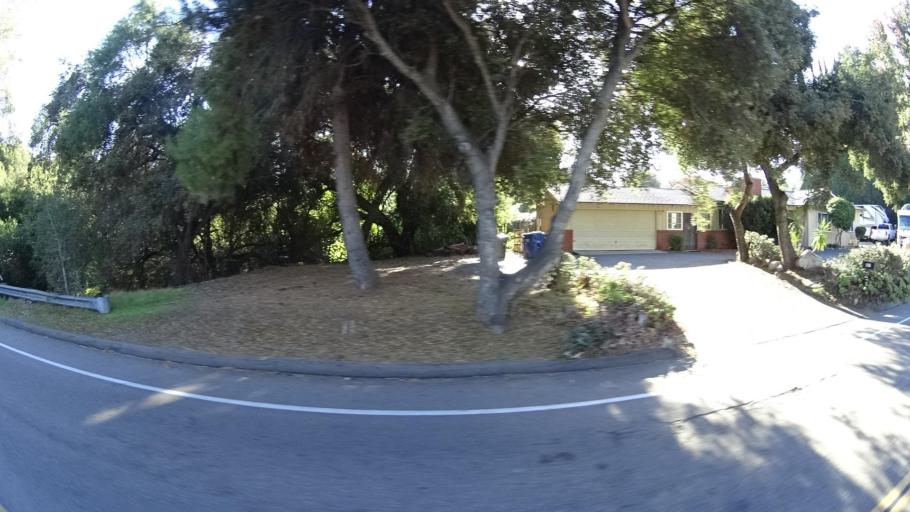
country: US
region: California
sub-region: San Diego County
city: Lakeside
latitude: 32.8391
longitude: -116.9052
